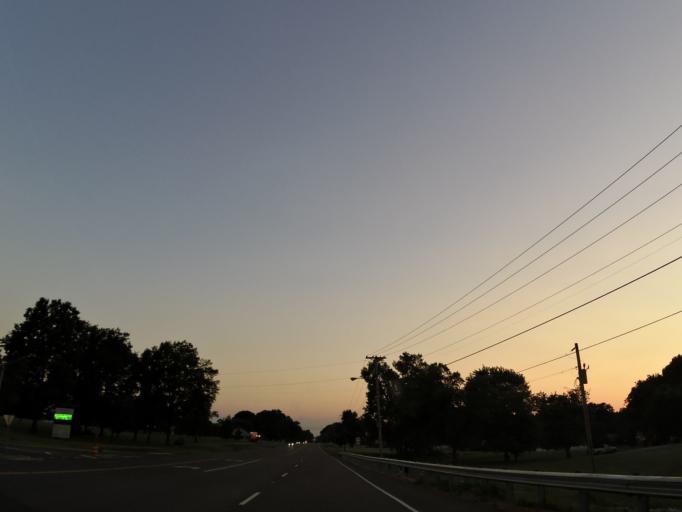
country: US
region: Tennessee
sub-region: Carroll County
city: McKenzie
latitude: 36.1396
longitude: -88.4916
